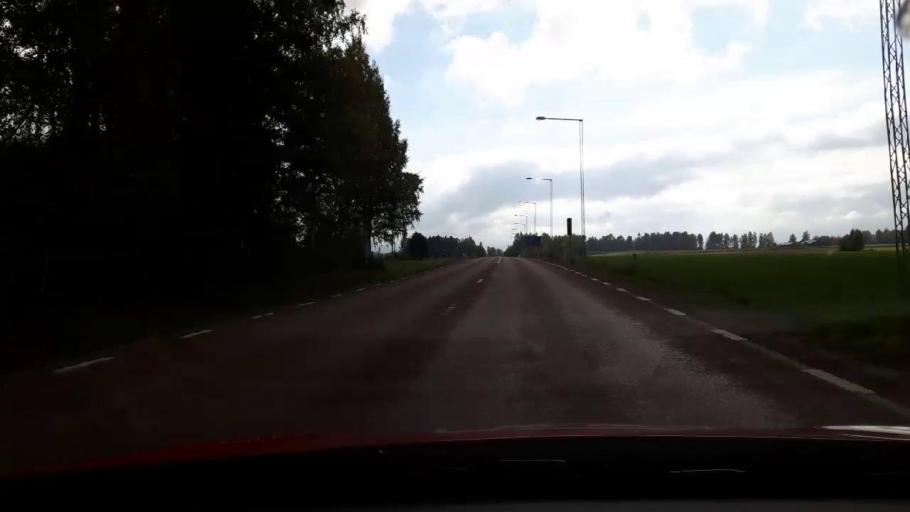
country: SE
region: Gaevleborg
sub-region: Bollnas Kommun
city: Arbra
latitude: 61.5438
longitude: 16.3547
